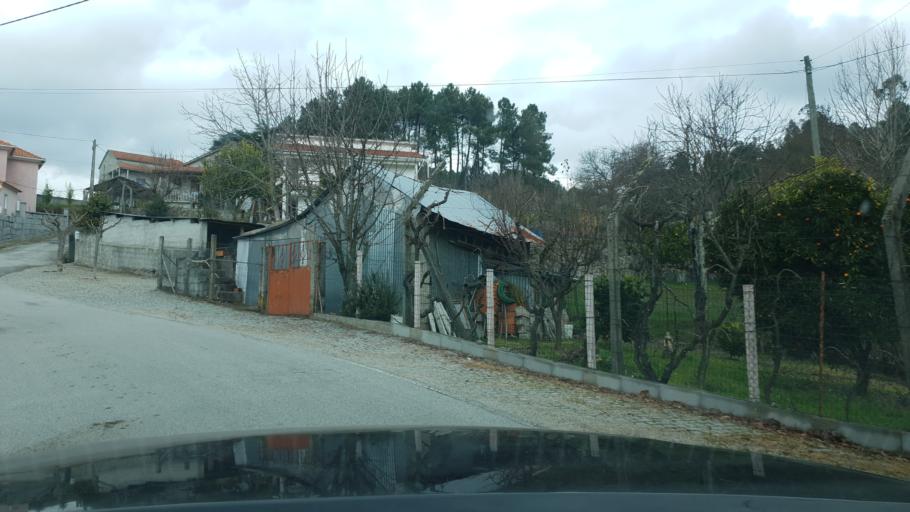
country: PT
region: Viseu
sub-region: Castro Daire
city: Castro Daire
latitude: 40.8804
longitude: -8.0117
